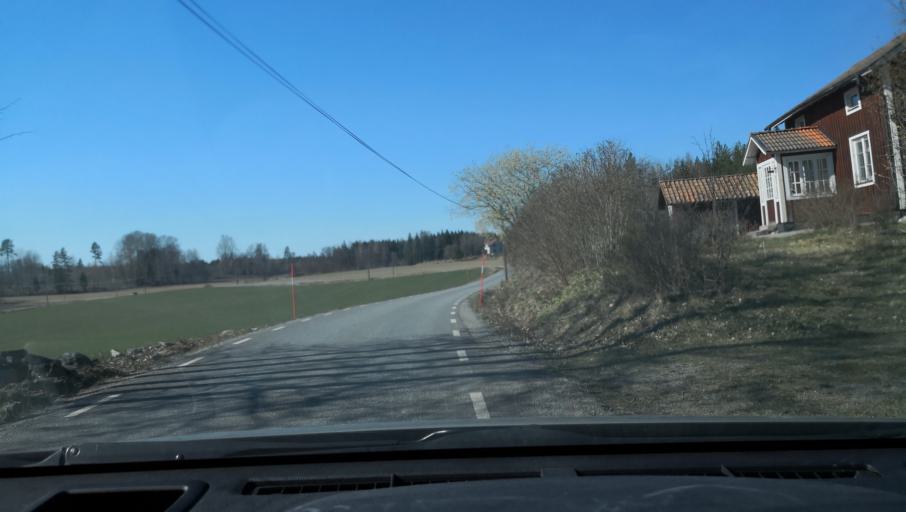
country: SE
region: Vaestmanland
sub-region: Sala Kommun
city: Sala
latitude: 59.9284
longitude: 16.4645
